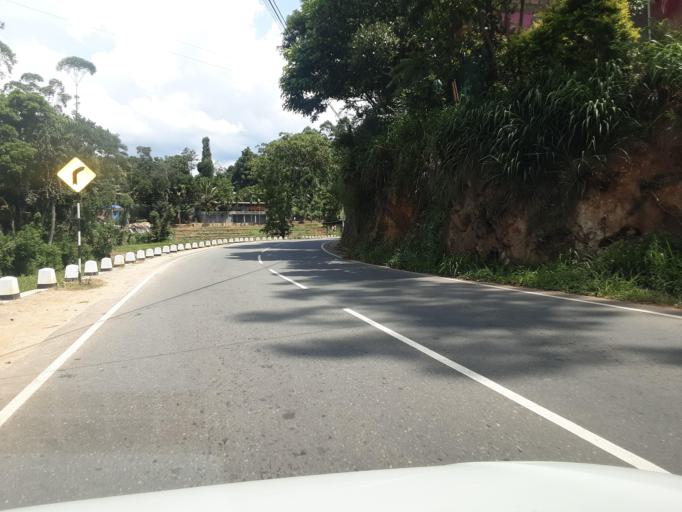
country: LK
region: Central
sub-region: Nuwara Eliya District
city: Nuwara Eliya
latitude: 6.9185
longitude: 80.9024
